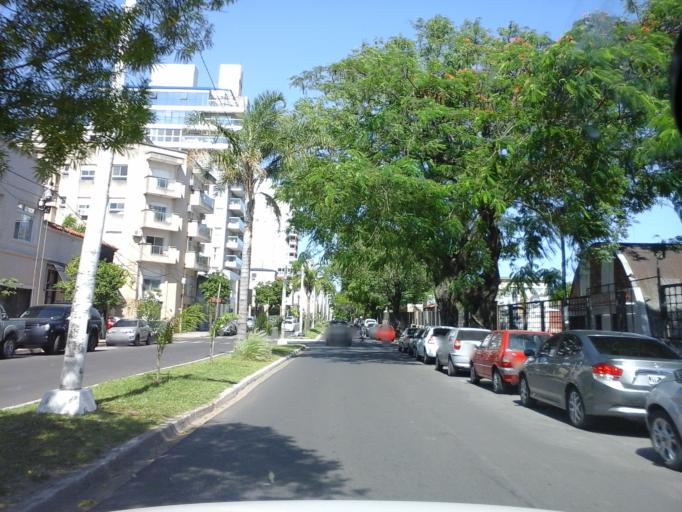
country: AR
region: Corrientes
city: Corrientes
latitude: -27.4612
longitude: -58.8309
